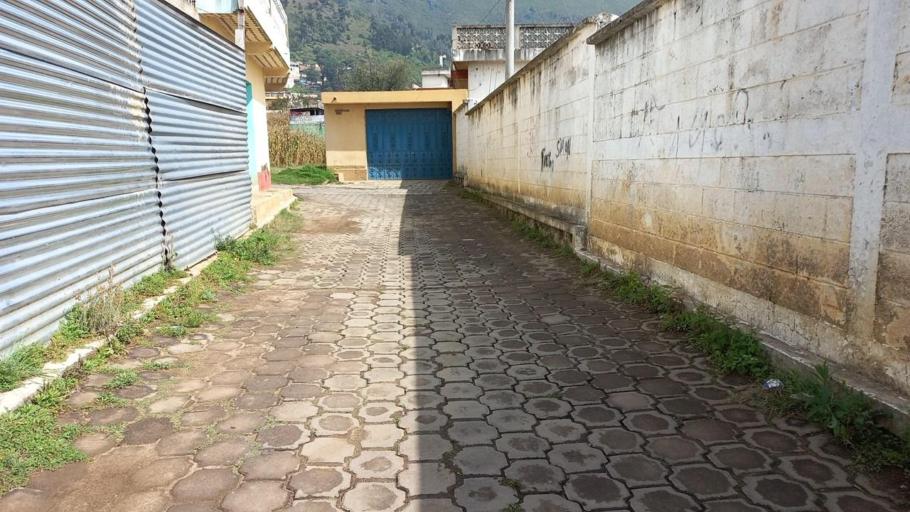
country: GT
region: Totonicapan
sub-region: Municipio de San Andres Xecul
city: San Andres Xecul
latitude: 14.9027
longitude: -91.4829
